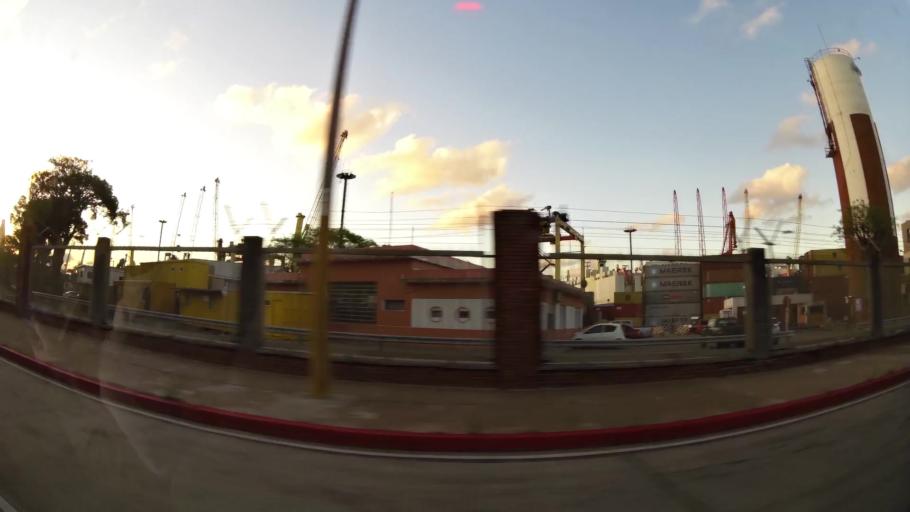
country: UY
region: Montevideo
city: Montevideo
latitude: -34.9028
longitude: -56.2062
